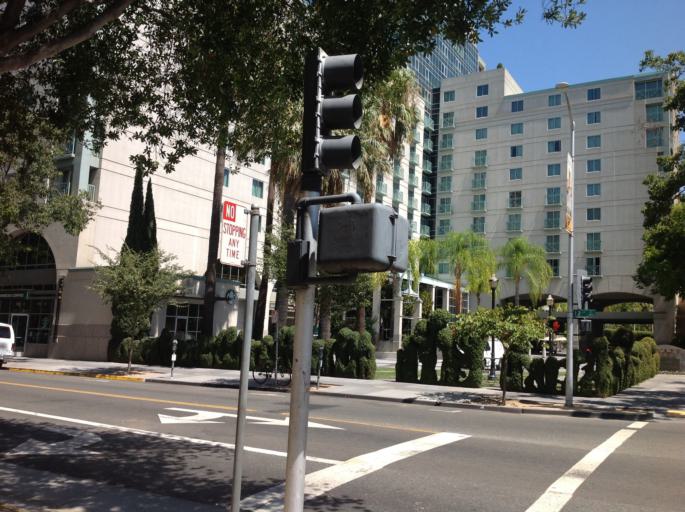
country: US
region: California
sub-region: Sacramento County
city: Sacramento
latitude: 38.5776
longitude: -121.4919
